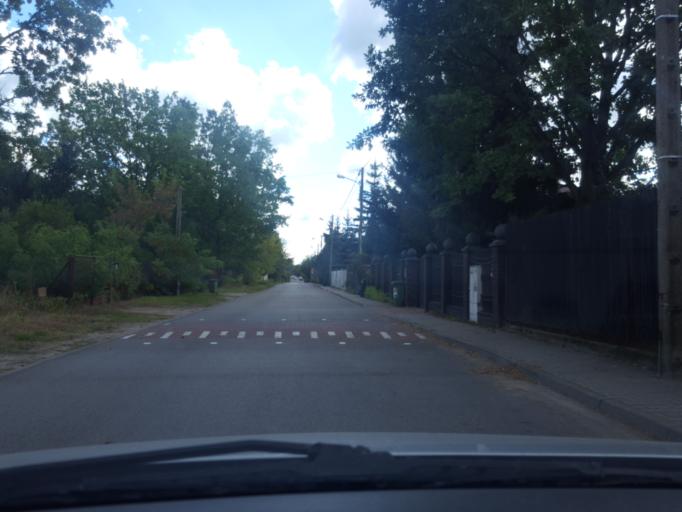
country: PL
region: Masovian Voivodeship
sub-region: Warszawa
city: Rembertow
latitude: 52.2728
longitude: 21.1623
